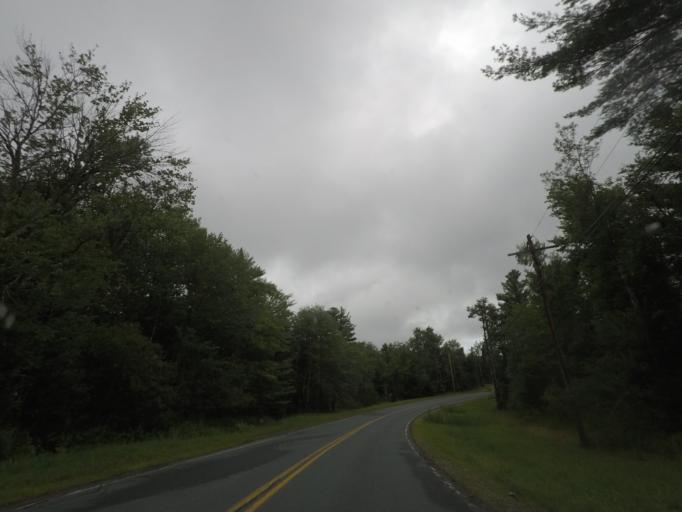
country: US
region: New York
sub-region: Rensselaer County
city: Poestenkill
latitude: 42.6927
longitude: -73.4240
